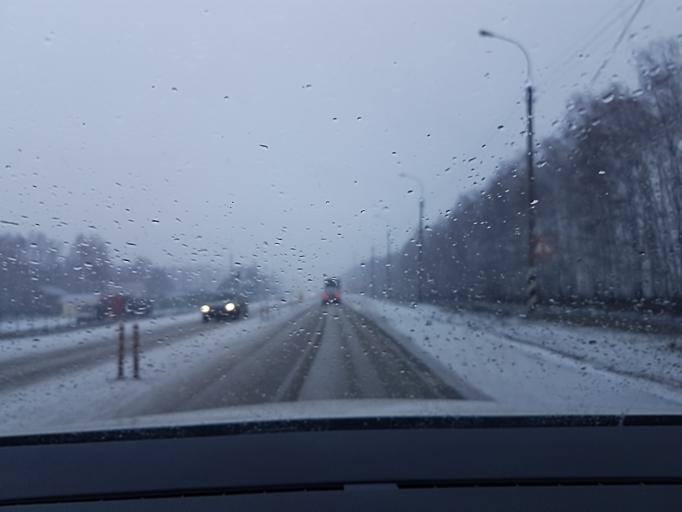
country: RU
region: Tambov
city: Pervomayskiy
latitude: 53.3112
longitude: 40.2203
